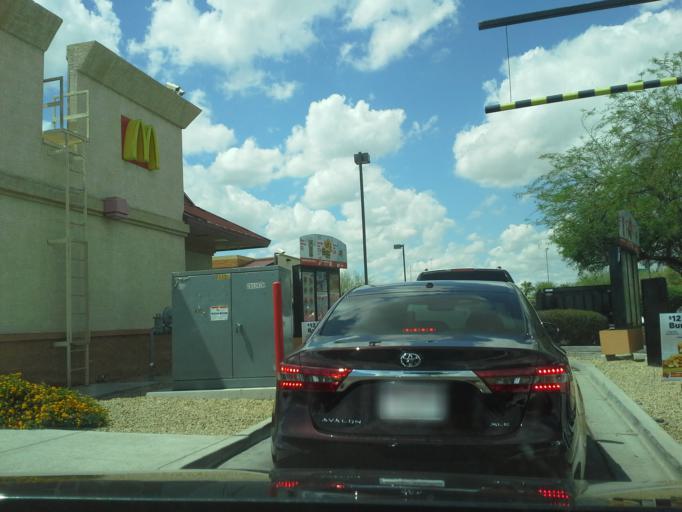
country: US
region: Arizona
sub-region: Maricopa County
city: Peoria
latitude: 33.6107
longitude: -112.2408
